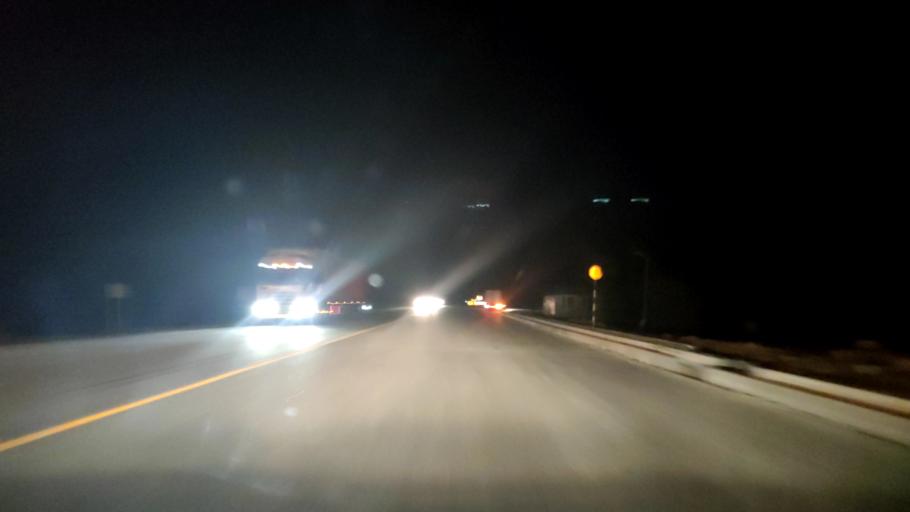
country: RU
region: Kursk
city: Gorshechnoye
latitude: 51.5531
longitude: 38.0335
